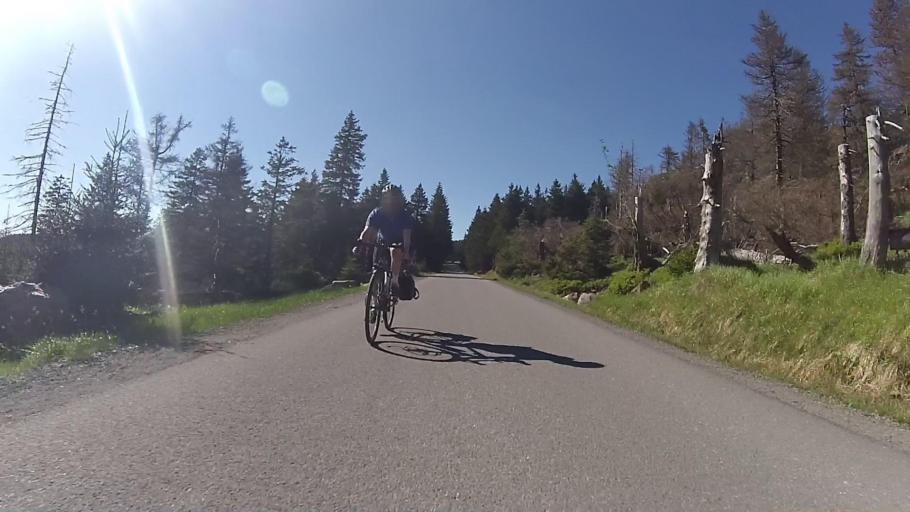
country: DE
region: Lower Saxony
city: Braunlage
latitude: 51.7883
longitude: 10.6261
